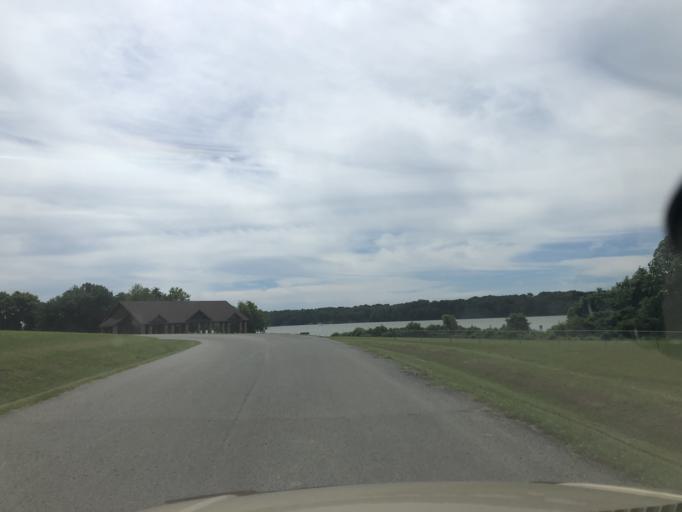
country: US
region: Tennessee
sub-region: Davidson County
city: Lakewood
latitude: 36.2503
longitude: -86.6061
